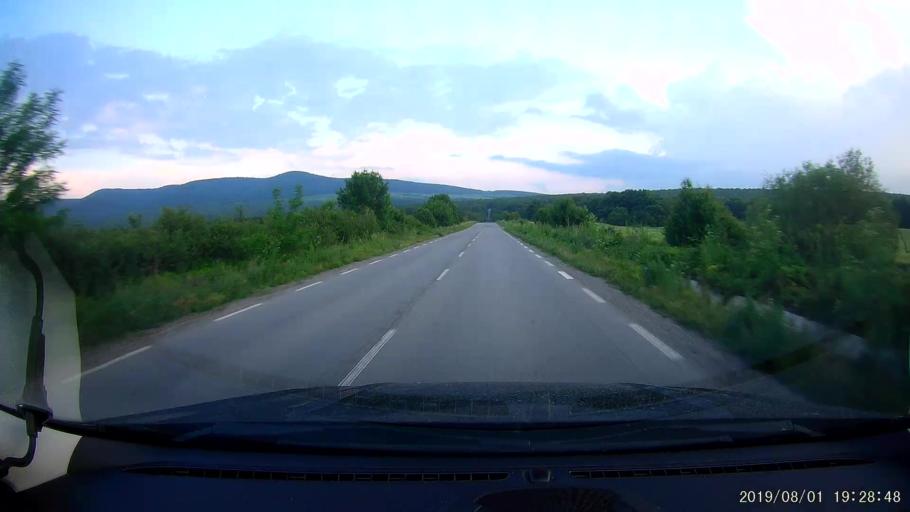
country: BG
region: Burgas
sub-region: Obshtina Sungurlare
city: Sungurlare
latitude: 42.8370
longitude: 26.9131
